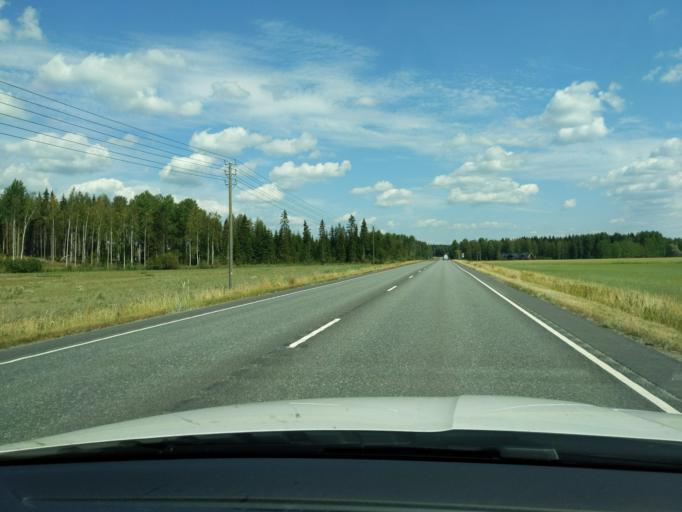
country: FI
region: Uusimaa
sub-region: Helsinki
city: Maentsaelae
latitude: 60.5951
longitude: 25.2489
